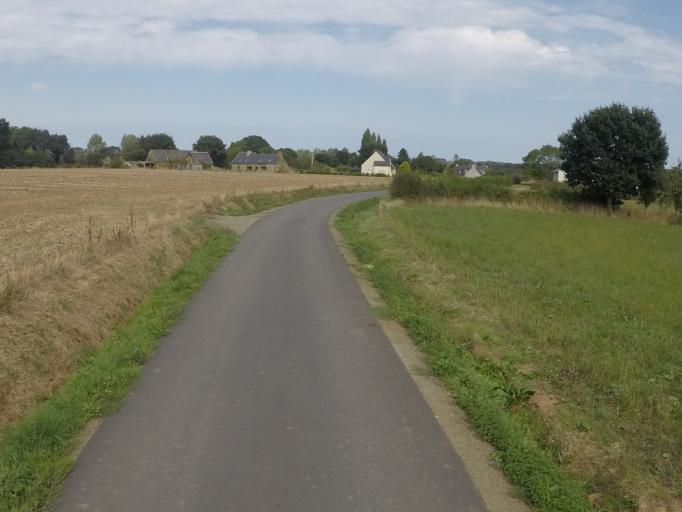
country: FR
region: Brittany
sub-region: Departement des Cotes-d'Armor
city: Goudelin
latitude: 48.5990
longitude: -2.9973
